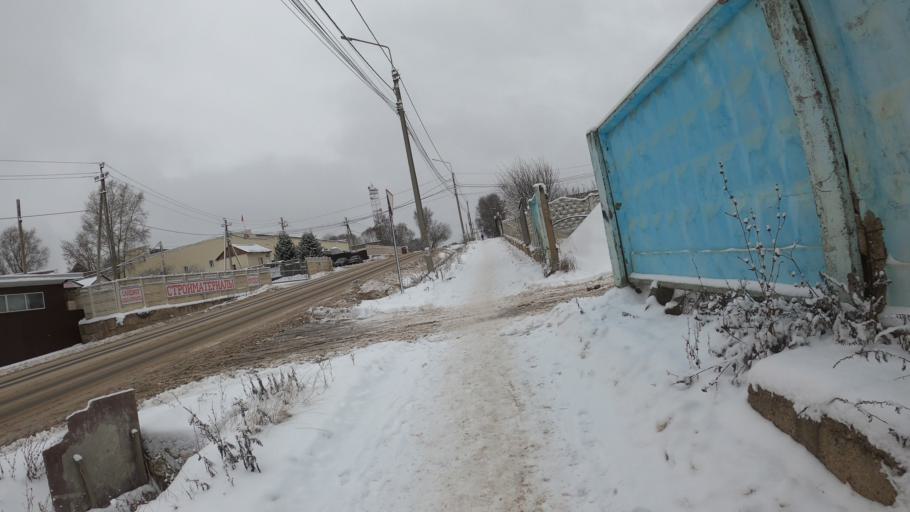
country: RU
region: Jaroslavl
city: Pereslavl'-Zalesskiy
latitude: 56.7415
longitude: 38.8915
